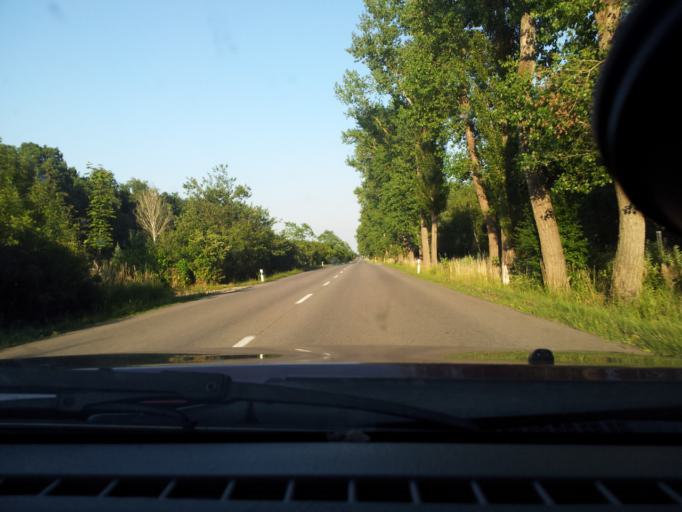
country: CZ
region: South Moravian
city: Dubnany
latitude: 48.8850
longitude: 17.0874
